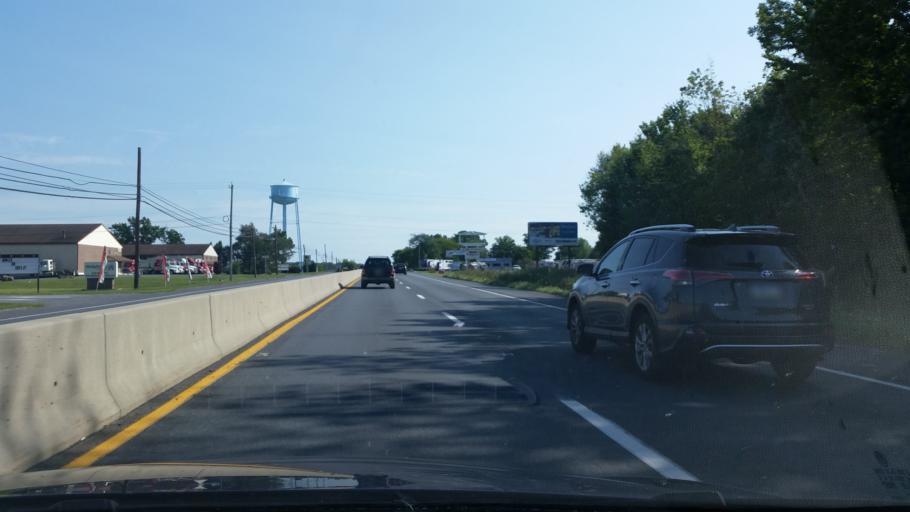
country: US
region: Pennsylvania
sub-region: Berks County
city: Shoemakersville
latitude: 40.5086
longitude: -75.9657
